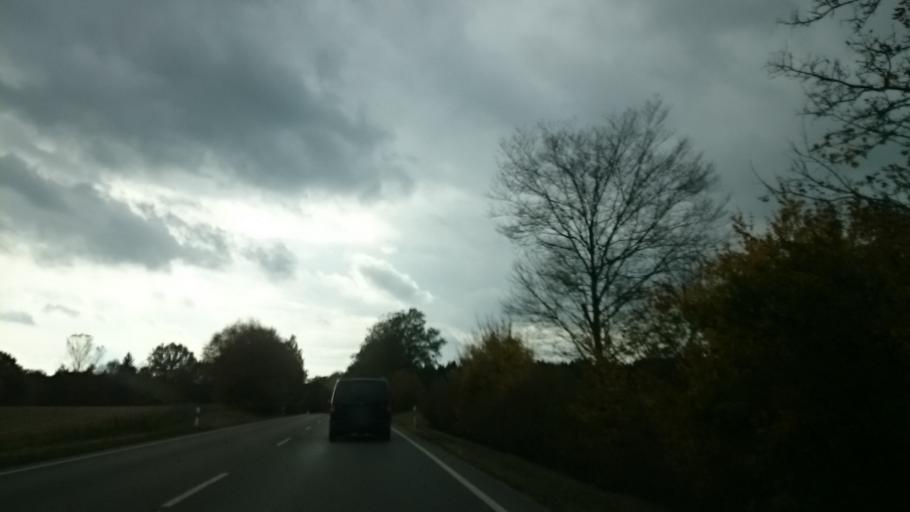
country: DE
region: Bavaria
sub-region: Regierungsbezirk Mittelfranken
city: Langenaltheim
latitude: 48.8955
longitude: 10.8791
